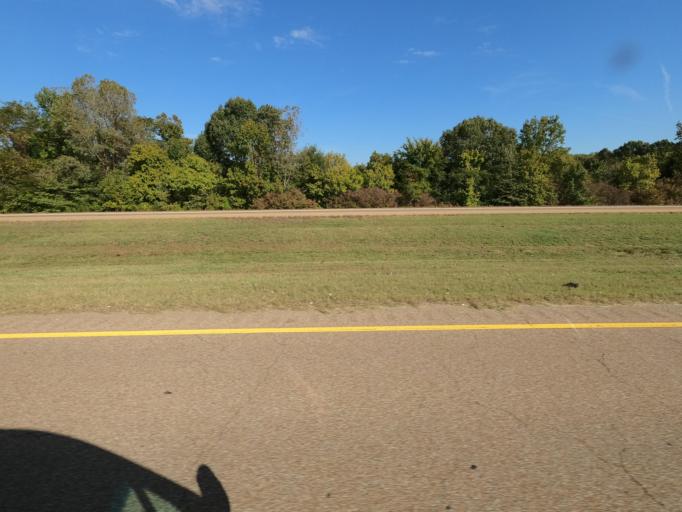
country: US
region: Tennessee
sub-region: Shelby County
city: Millington
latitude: 35.3303
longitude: -89.9139
